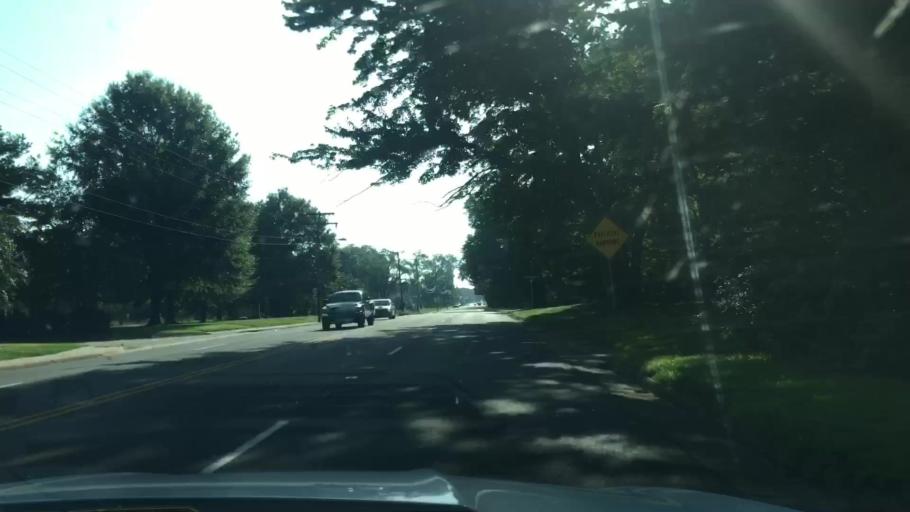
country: US
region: Virginia
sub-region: Richmond County
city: Warsaw
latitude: 37.9588
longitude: -76.7676
